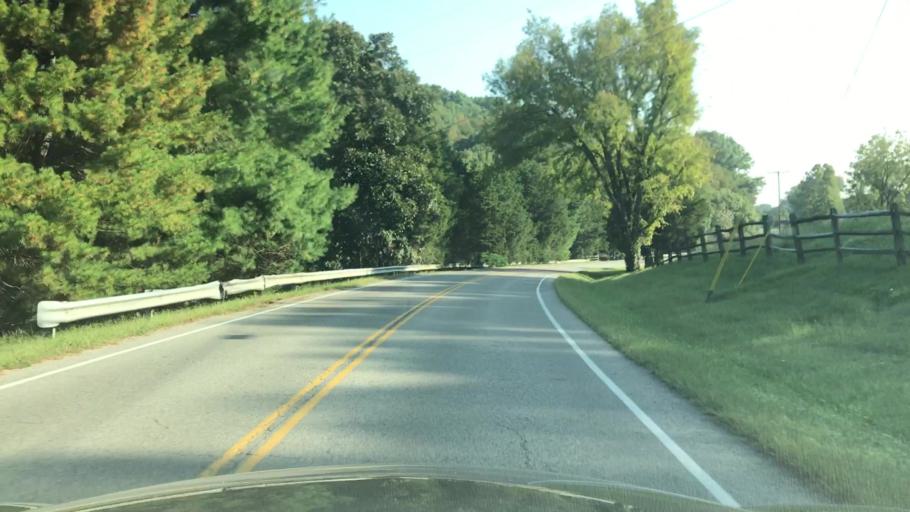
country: US
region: Tennessee
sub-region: Davidson County
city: Forest Hills
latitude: 36.0350
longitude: -86.9144
